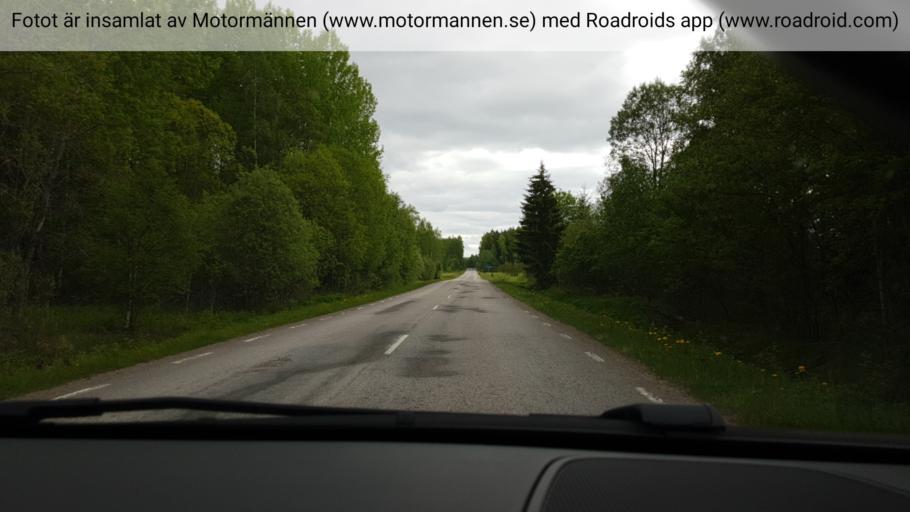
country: SE
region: Uppsala
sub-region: Heby Kommun
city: Tarnsjo
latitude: 60.1446
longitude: 16.9745
